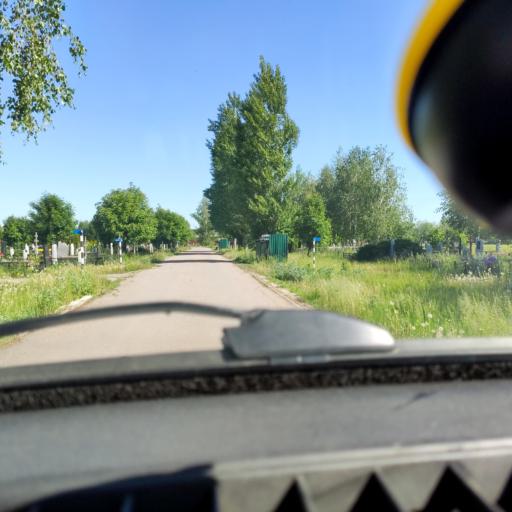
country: RU
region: Samara
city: Tol'yatti
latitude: 53.5743
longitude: 49.4274
